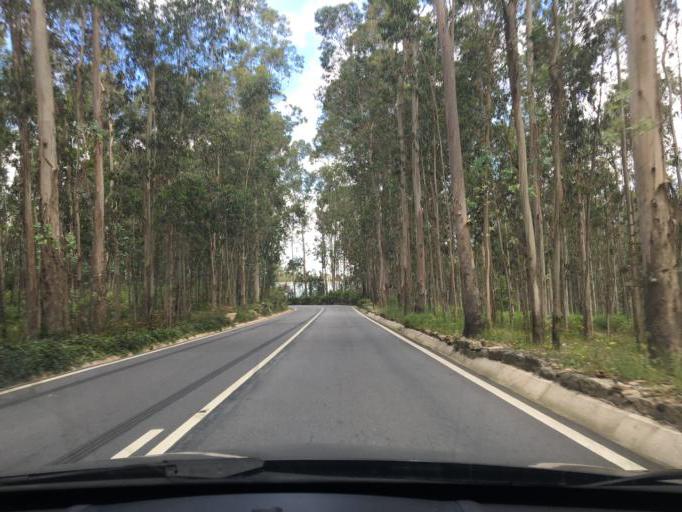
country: PT
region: Porto
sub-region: Maia
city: Anta
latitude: 41.2892
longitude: -8.6074
